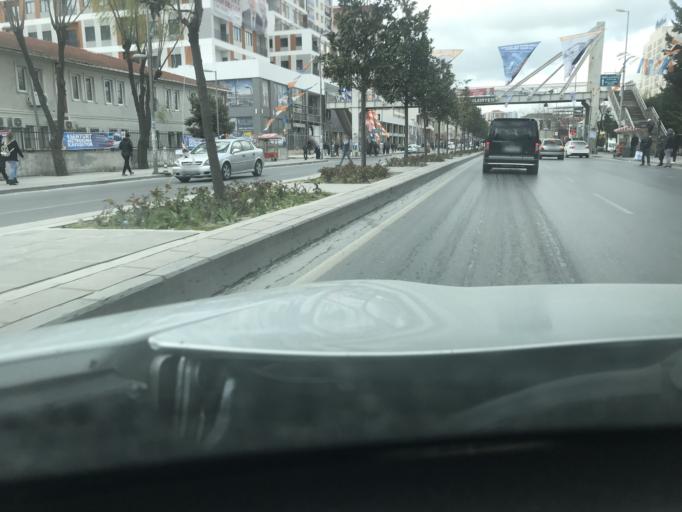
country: TR
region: Istanbul
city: Esenyurt
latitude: 41.0391
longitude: 28.6779
